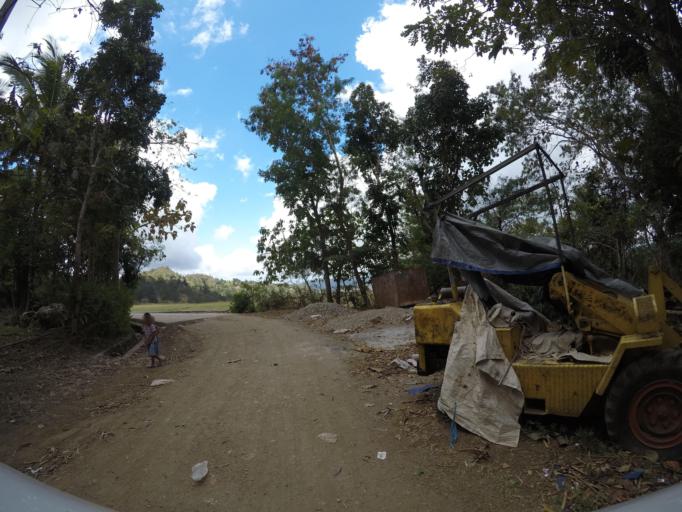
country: TL
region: Lautem
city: Lospalos
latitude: -8.5581
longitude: 126.8290
